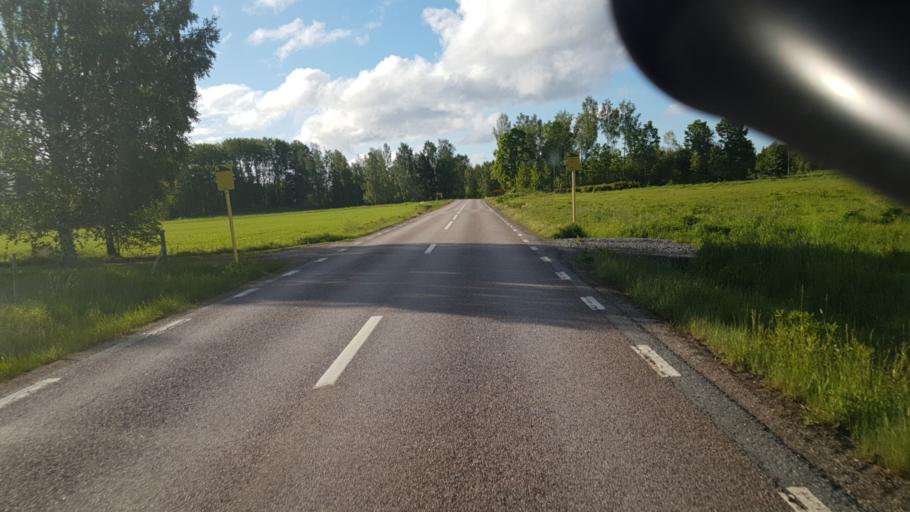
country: SE
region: Vaermland
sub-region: Arvika Kommun
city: Arvika
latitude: 59.6080
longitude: 12.5284
